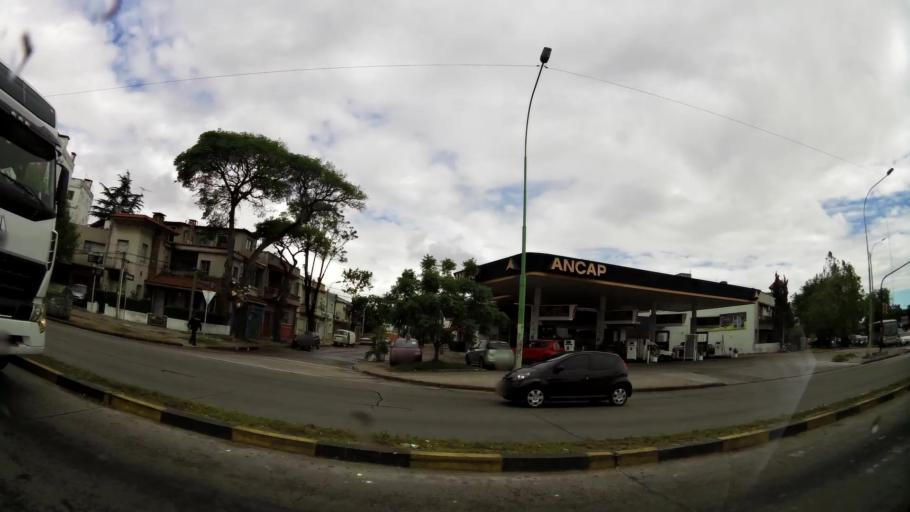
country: UY
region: Montevideo
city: Montevideo
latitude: -34.8702
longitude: -56.1740
